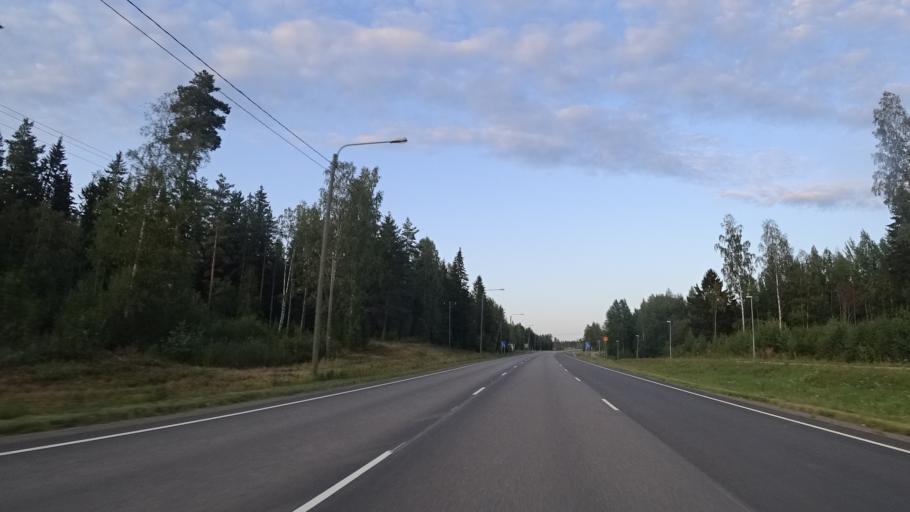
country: FI
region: Kymenlaakso
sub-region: Kotka-Hamina
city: Virojoki
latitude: 60.5922
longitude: 27.7565
